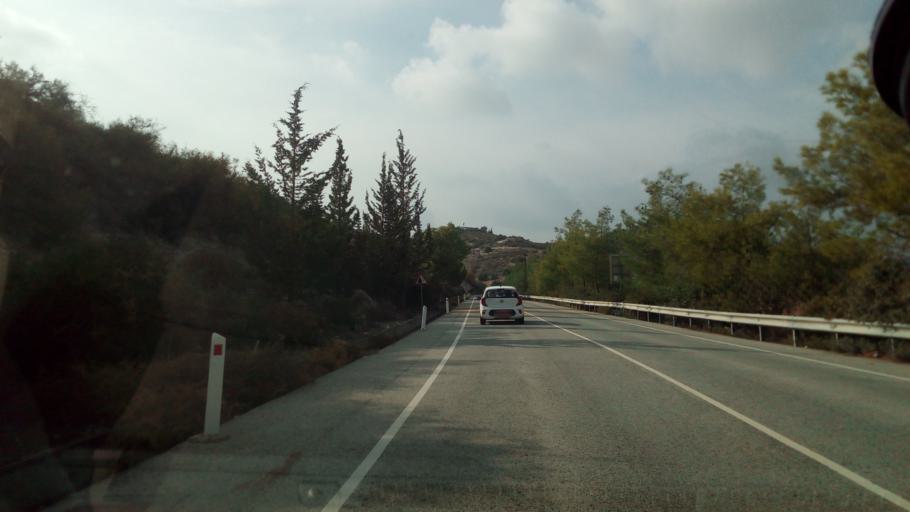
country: CY
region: Larnaka
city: Kofinou
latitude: 34.8273
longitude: 33.3604
